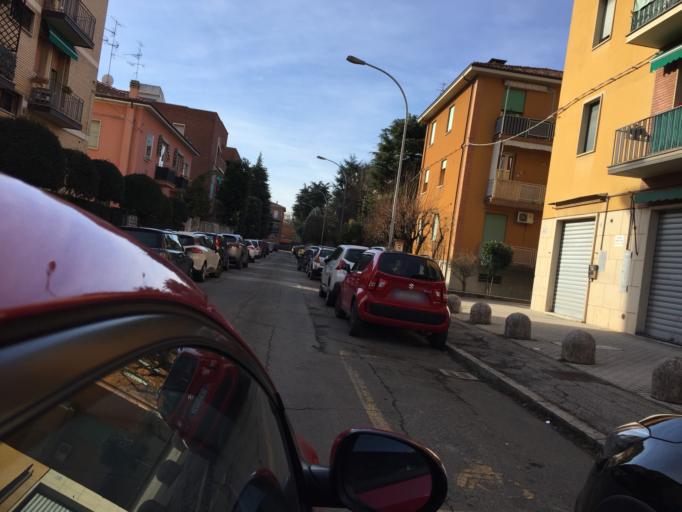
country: IT
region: Emilia-Romagna
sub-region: Provincia di Bologna
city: Casalecchio di Reno
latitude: 44.4998
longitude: 11.2948
